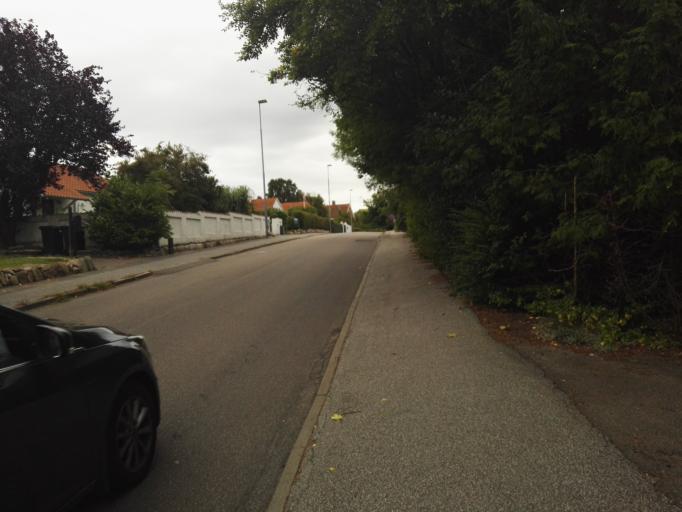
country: DK
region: Zealand
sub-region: Odsherred Kommune
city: Nykobing Sjaelland
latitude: 55.9293
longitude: 11.6688
